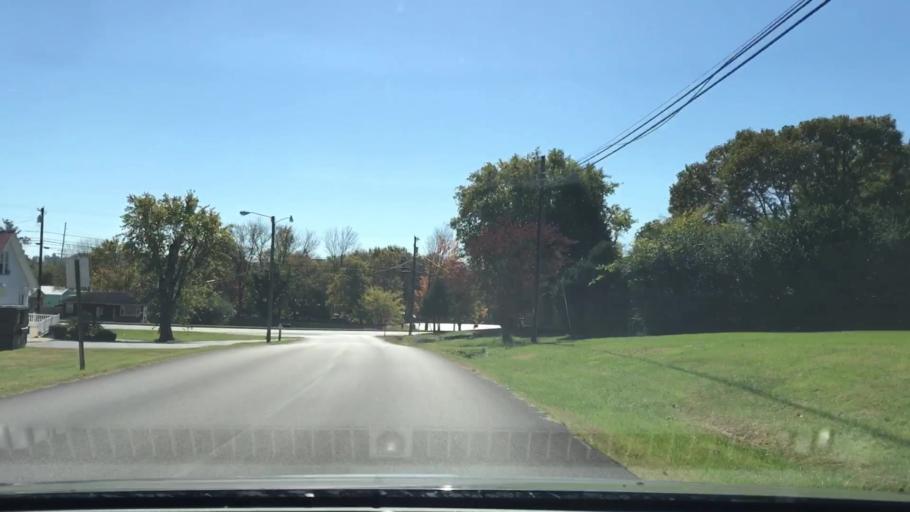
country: US
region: Kentucky
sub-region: Barren County
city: Glasgow
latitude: 36.9898
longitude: -85.9338
